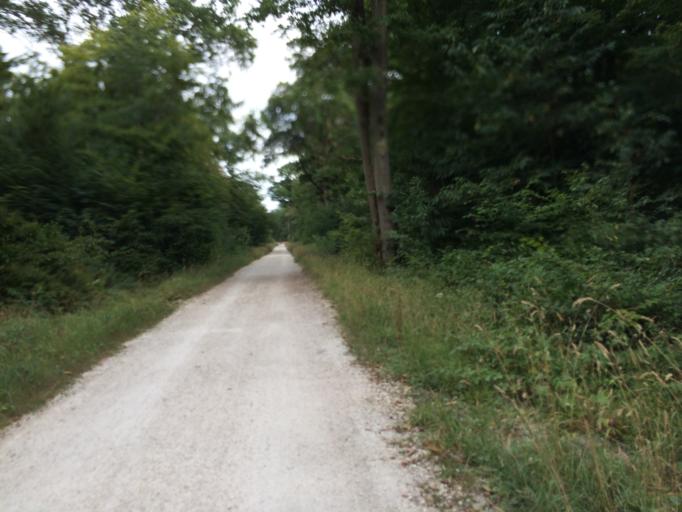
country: FR
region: Ile-de-France
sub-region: Departement de l'Essonne
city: Quincy-sous-Senart
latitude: 48.6565
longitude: 2.5344
